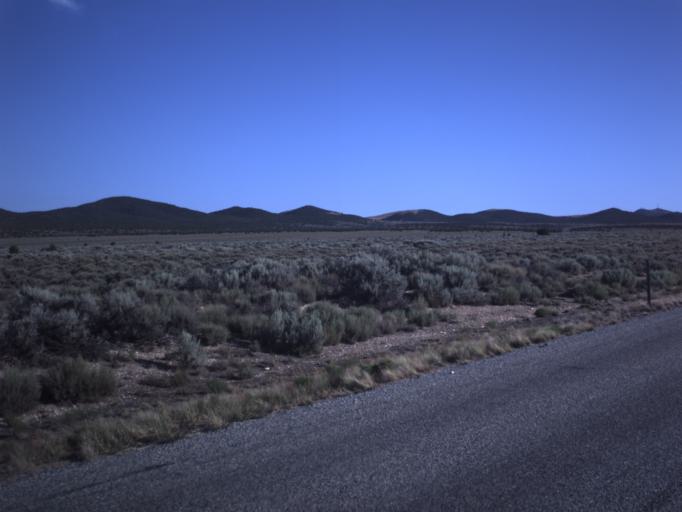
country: US
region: Utah
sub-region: Iron County
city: Enoch
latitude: 38.0006
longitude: -112.9982
